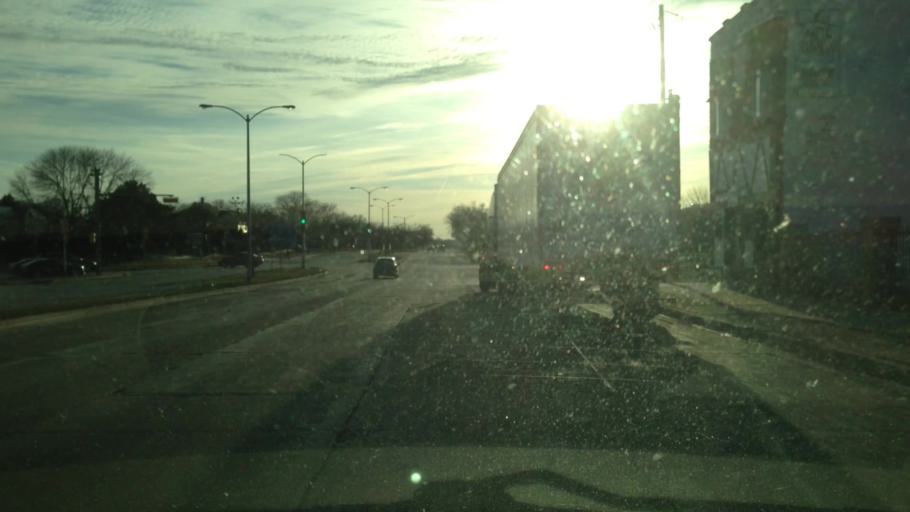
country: US
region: Wisconsin
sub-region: Milwaukee County
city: Milwaukee
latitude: 43.0527
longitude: -87.9272
